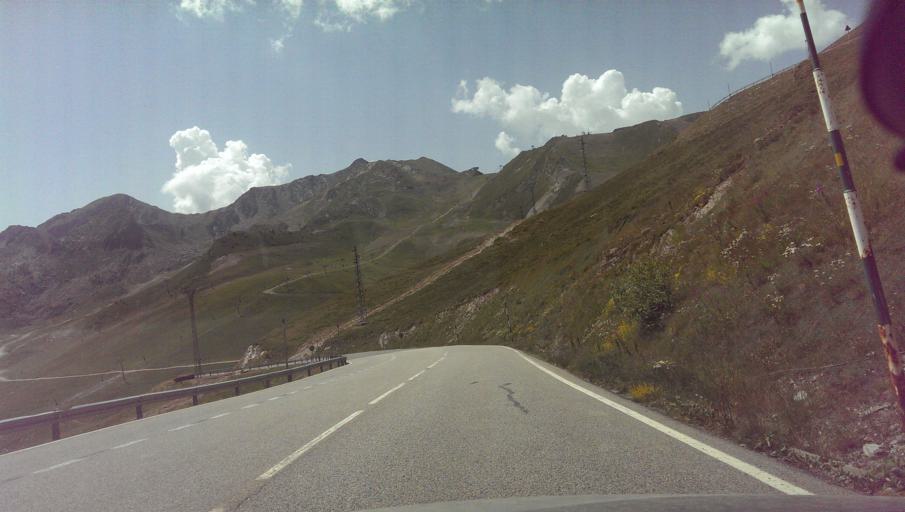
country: AD
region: Encamp
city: Pas de la Casa
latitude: 42.5415
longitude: 1.7276
